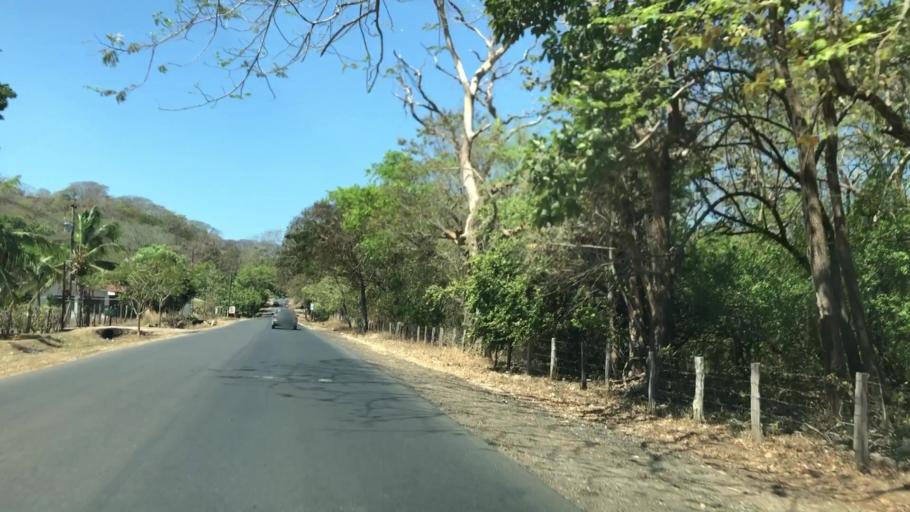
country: CR
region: Guanacaste
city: Belen
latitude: 10.3666
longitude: -85.7900
